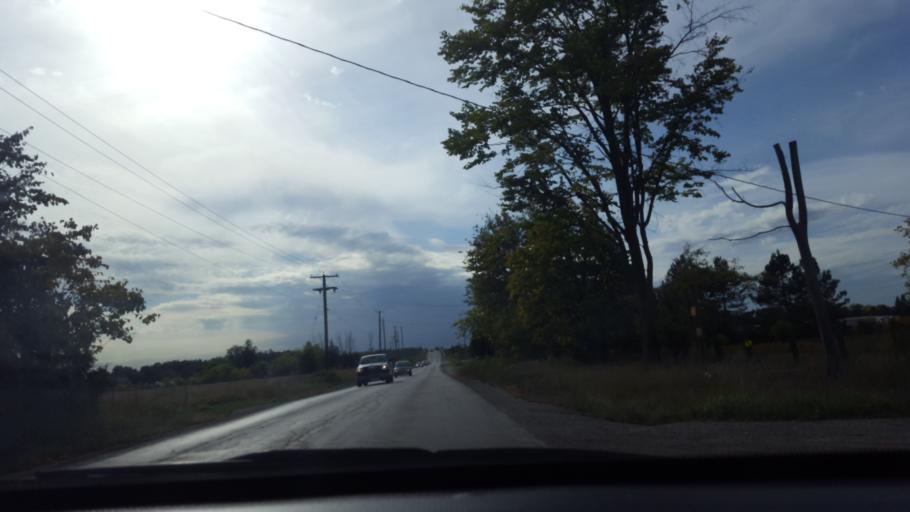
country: CA
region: Ontario
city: Vaughan
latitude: 43.9036
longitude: -79.5558
